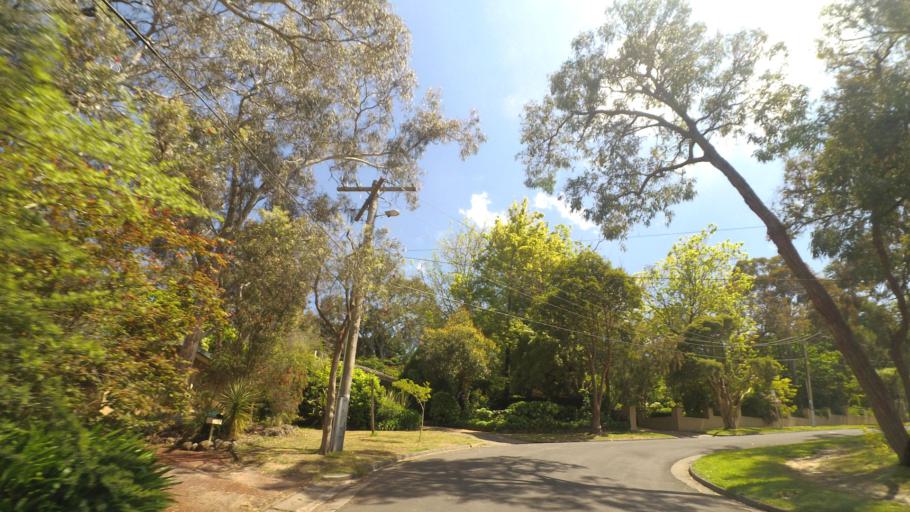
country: AU
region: Victoria
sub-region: Maroondah
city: Heathmont
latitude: -37.8298
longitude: 145.2539
